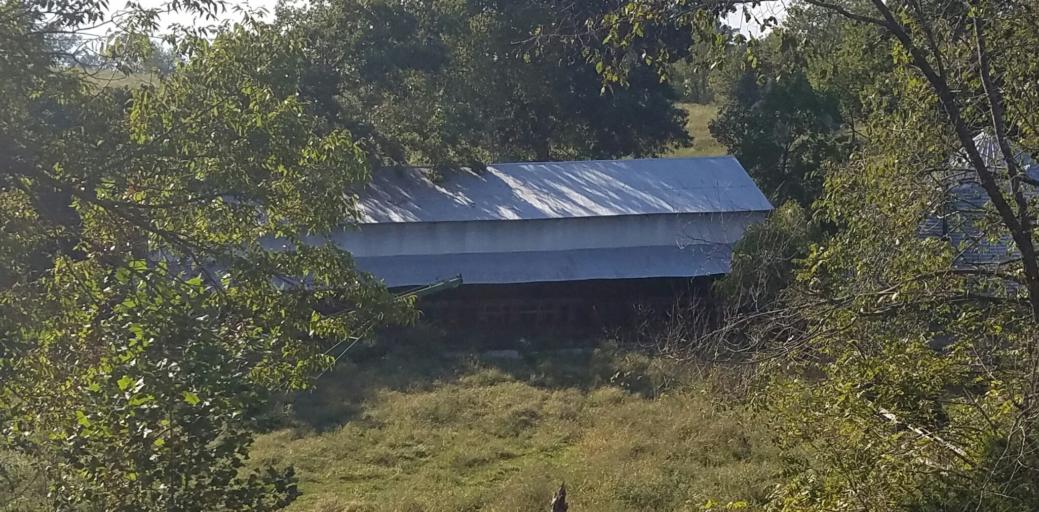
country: US
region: Missouri
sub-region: Moniteau County
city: California
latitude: 38.7283
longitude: -92.6383
